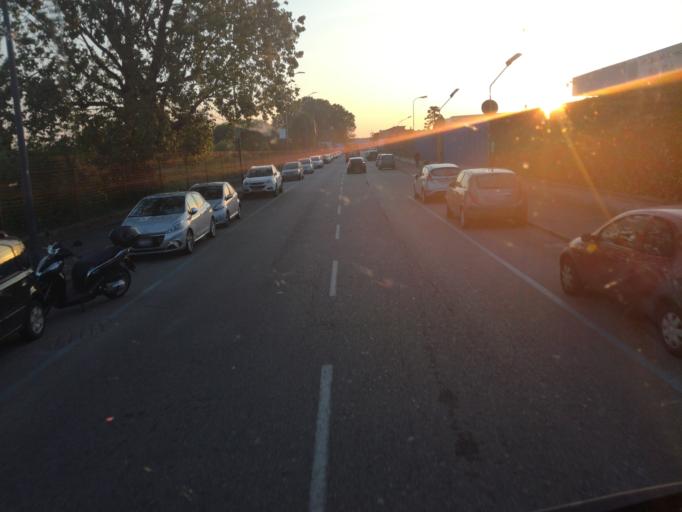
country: IT
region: Lombardy
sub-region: Citta metropolitana di Milano
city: Cormano
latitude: 45.5317
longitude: 9.1597
